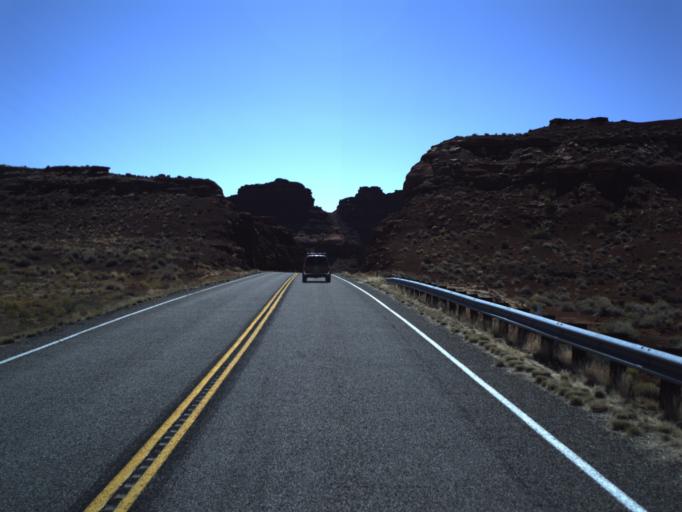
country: US
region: Utah
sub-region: San Juan County
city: Blanding
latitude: 37.8572
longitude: -110.3543
